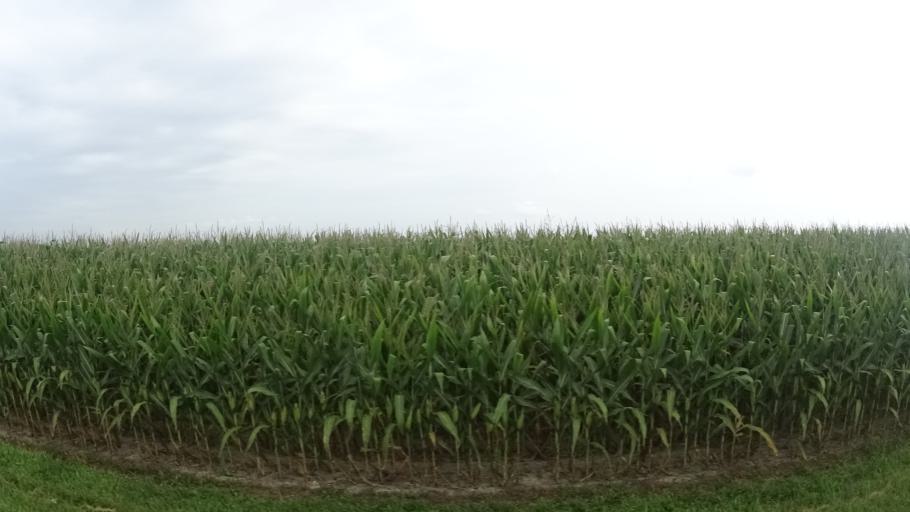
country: US
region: Indiana
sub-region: Madison County
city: Lapel
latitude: 40.0520
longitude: -85.8240
